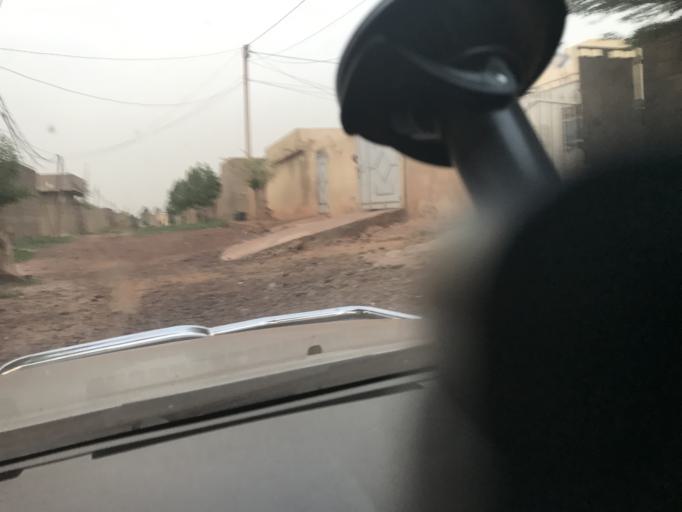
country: ML
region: Bamako
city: Bamako
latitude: 12.6495
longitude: -7.8793
